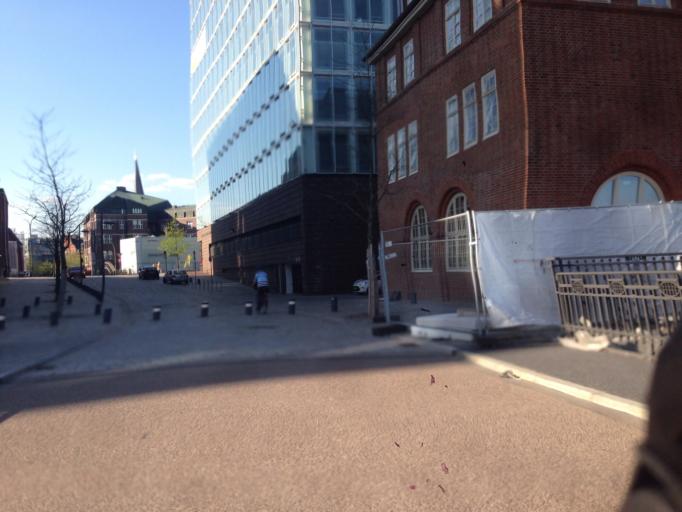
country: DE
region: Hamburg
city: Altstadt
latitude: 53.5445
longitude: 10.0032
